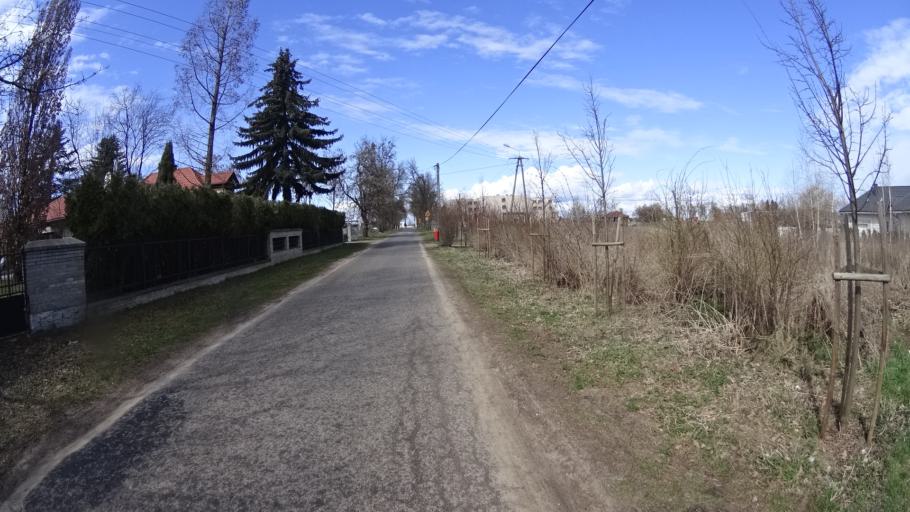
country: PL
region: Masovian Voivodeship
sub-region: Powiat warszawski zachodni
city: Jozefow
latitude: 52.2084
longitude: 20.6827
